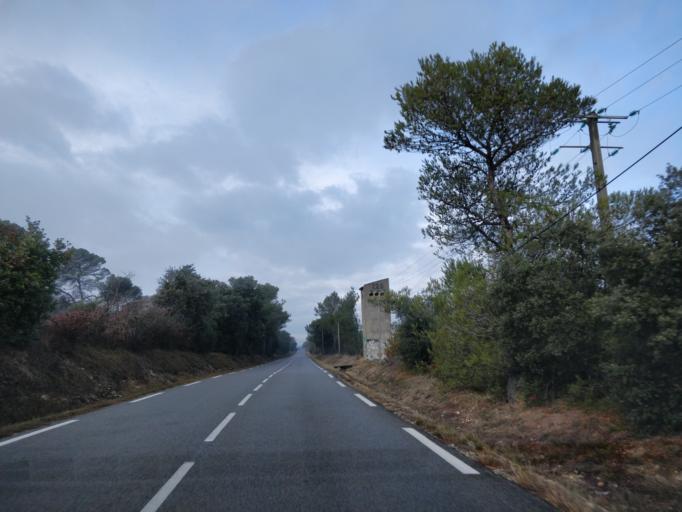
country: FR
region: Languedoc-Roussillon
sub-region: Departement du Gard
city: Caveirac
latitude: 43.8720
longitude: 4.2752
